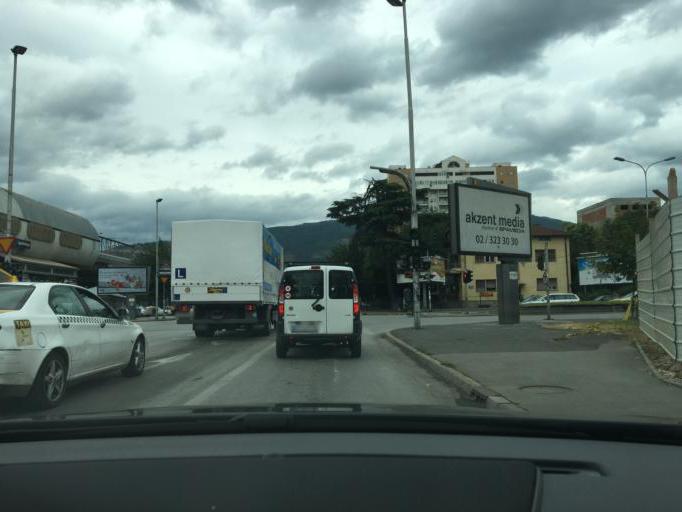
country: MK
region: Karpos
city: Skopje
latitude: 41.9920
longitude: 21.4457
